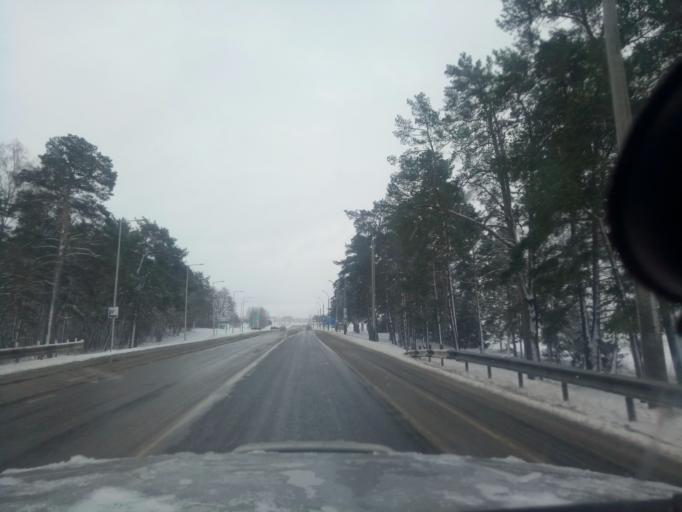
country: BY
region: Minsk
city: Nyasvizh
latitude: 53.2431
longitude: 26.6288
